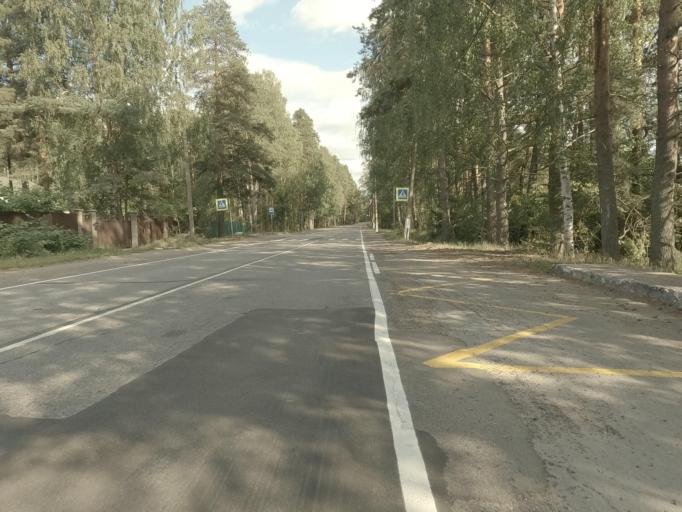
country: RU
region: Leningrad
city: Kamennogorsk
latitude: 60.9454
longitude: 29.1427
